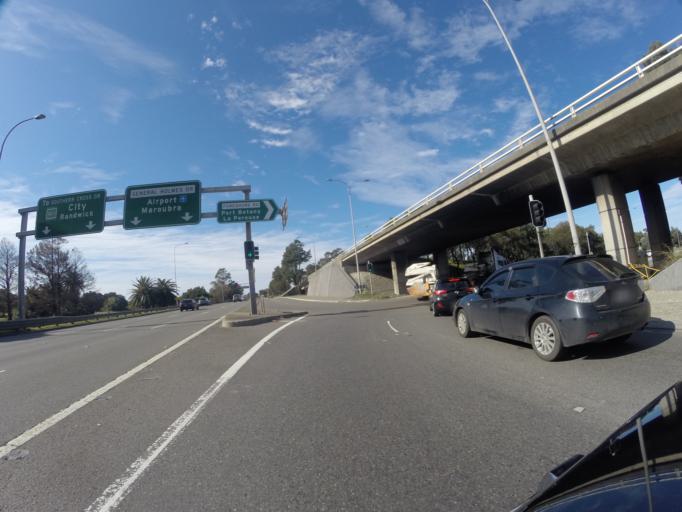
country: AU
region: New South Wales
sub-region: Botany Bay
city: Botany
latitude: -33.9446
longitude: 151.1879
